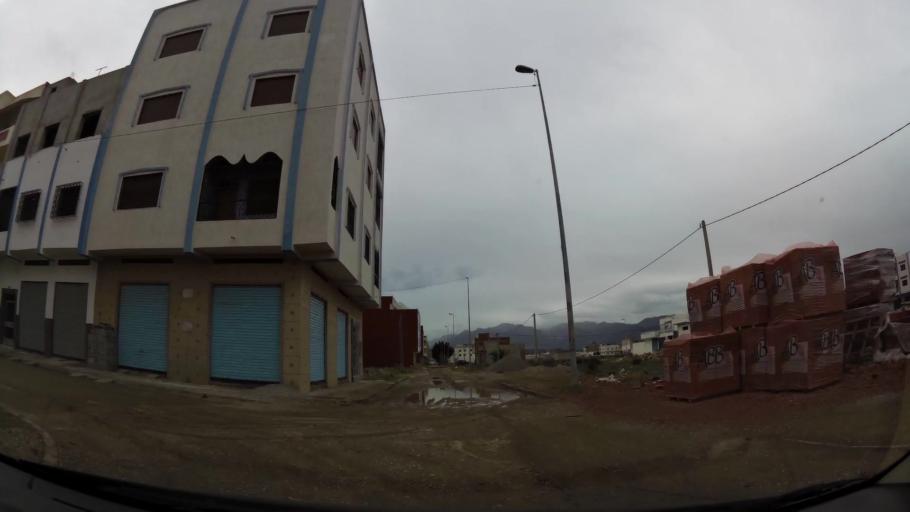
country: MA
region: Tanger-Tetouan
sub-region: Tetouan
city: Martil
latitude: 35.6155
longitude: -5.3032
